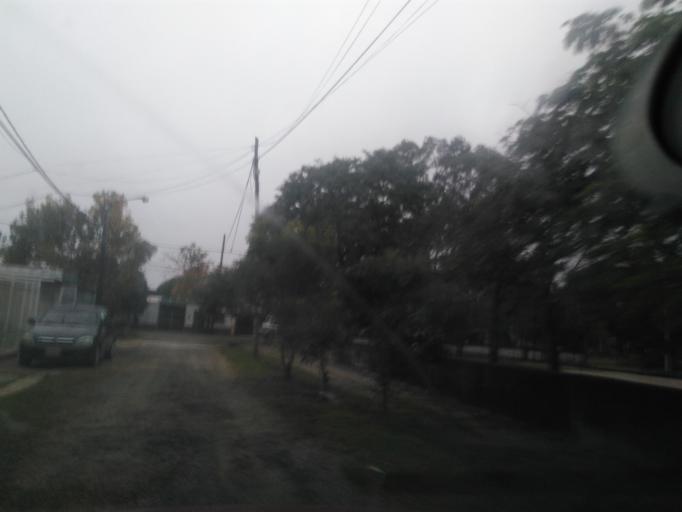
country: AR
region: Chaco
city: Resistencia
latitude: -27.4724
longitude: -58.9903
